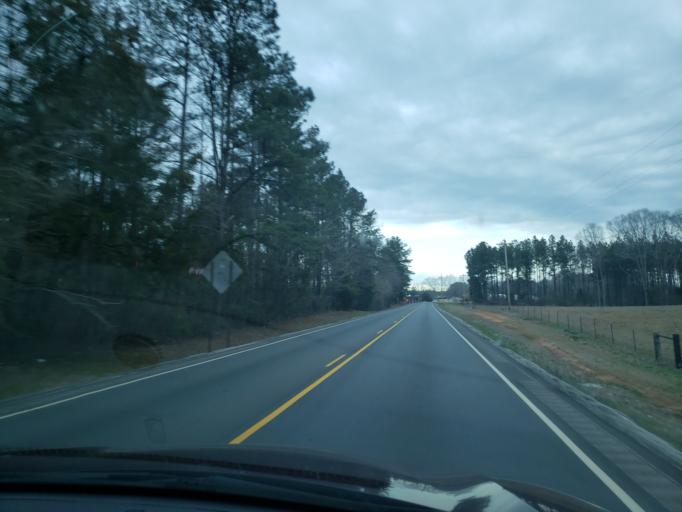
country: US
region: Alabama
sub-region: Randolph County
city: Roanoke
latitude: 33.0848
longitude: -85.3372
